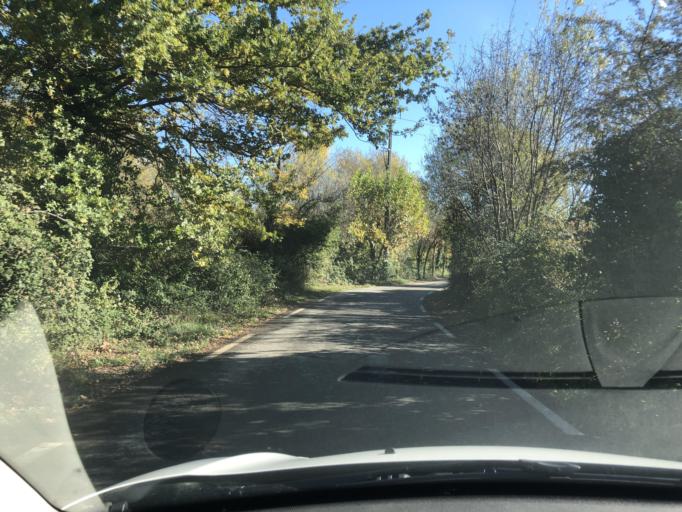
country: FR
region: Provence-Alpes-Cote d'Azur
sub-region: Departement du Vaucluse
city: Althen-des-Paluds
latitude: 43.9792
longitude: 4.9432
